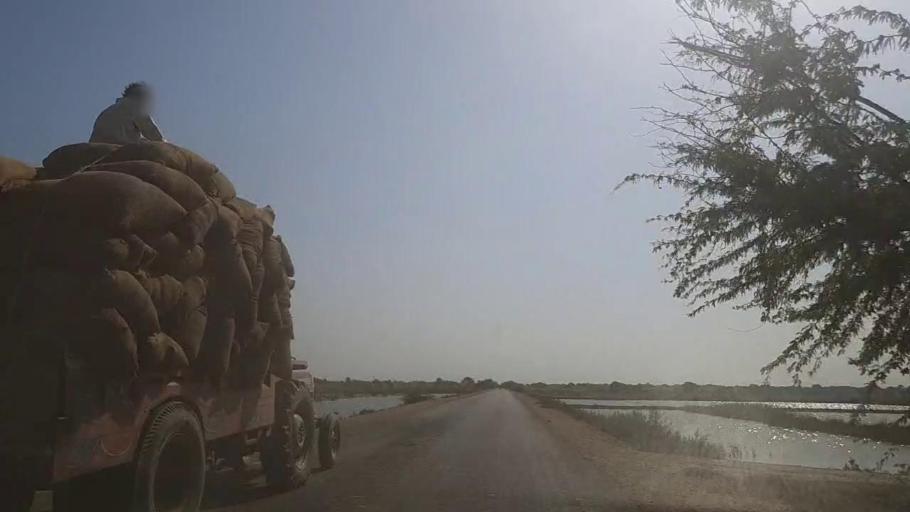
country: PK
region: Sindh
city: Mirpur Batoro
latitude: 24.5807
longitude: 68.2892
